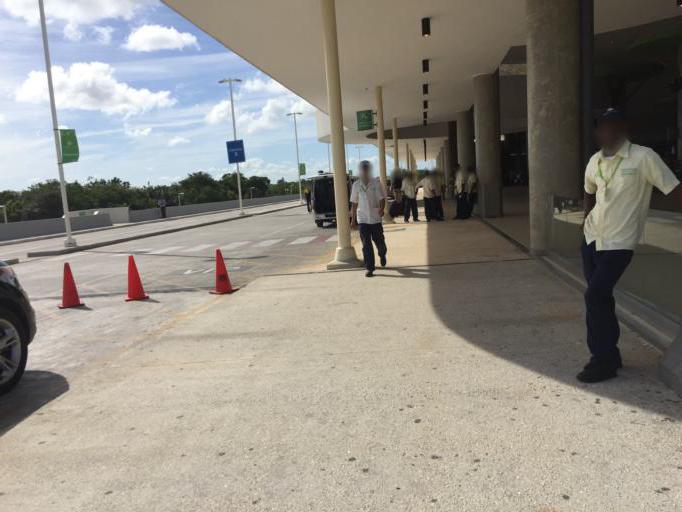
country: DO
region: San Juan
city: Punta Cana
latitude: 18.5621
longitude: -68.3676
